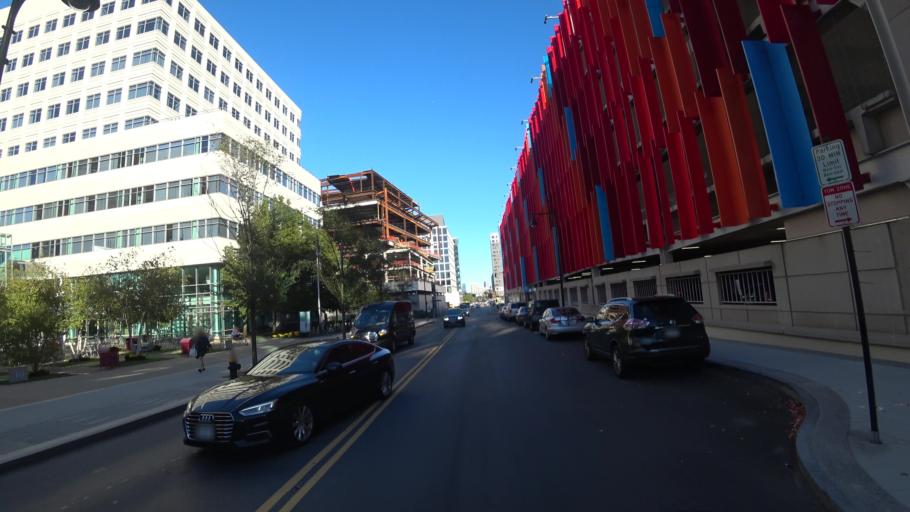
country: US
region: Massachusetts
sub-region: Norfolk County
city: Brookline
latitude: 42.3573
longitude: -71.1472
